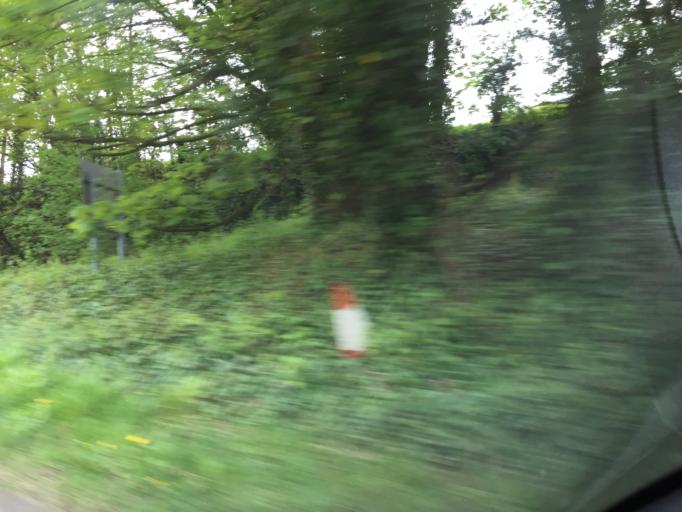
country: GB
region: England
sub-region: Bath and North East Somerset
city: Peasedown Saint John
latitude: 51.3354
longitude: -2.4099
